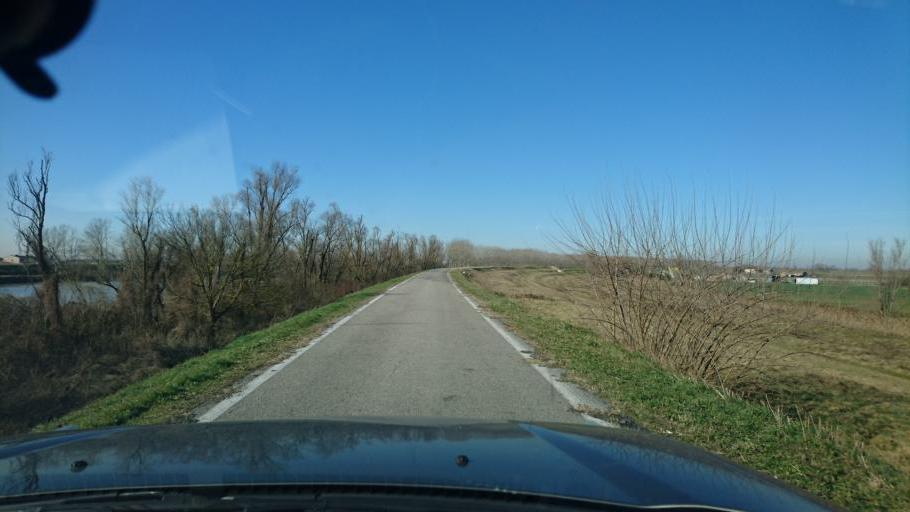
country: IT
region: Emilia-Romagna
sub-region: Provincia di Ferrara
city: Mesola
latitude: 44.9260
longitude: 12.1949
